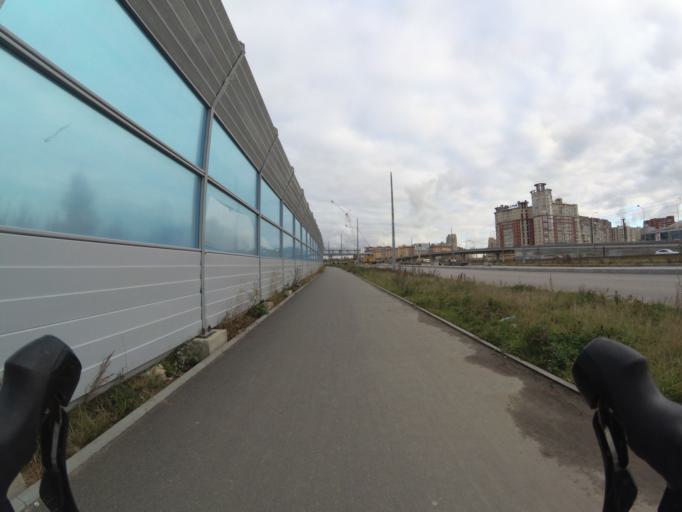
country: RU
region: Leningrad
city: Untolovo
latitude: 59.9909
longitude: 30.1857
